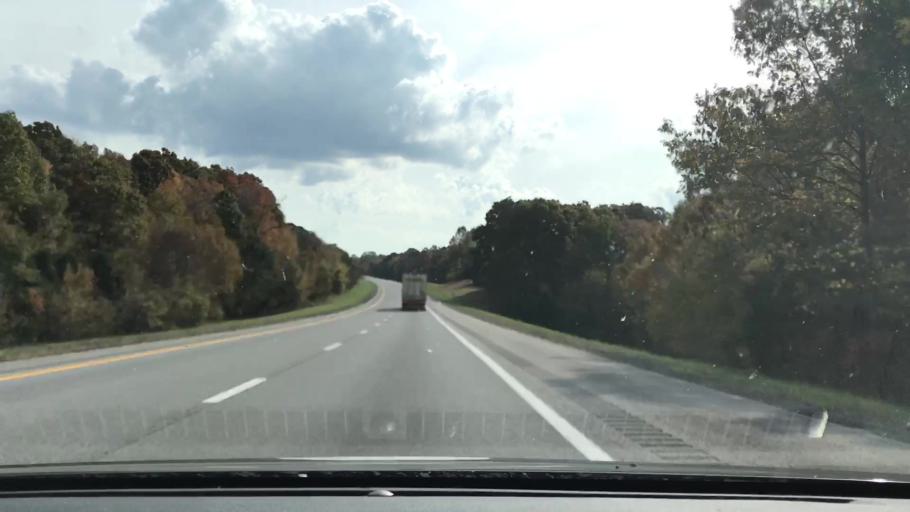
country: US
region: Kentucky
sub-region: Caldwell County
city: Princeton
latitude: 37.0035
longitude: -87.9669
